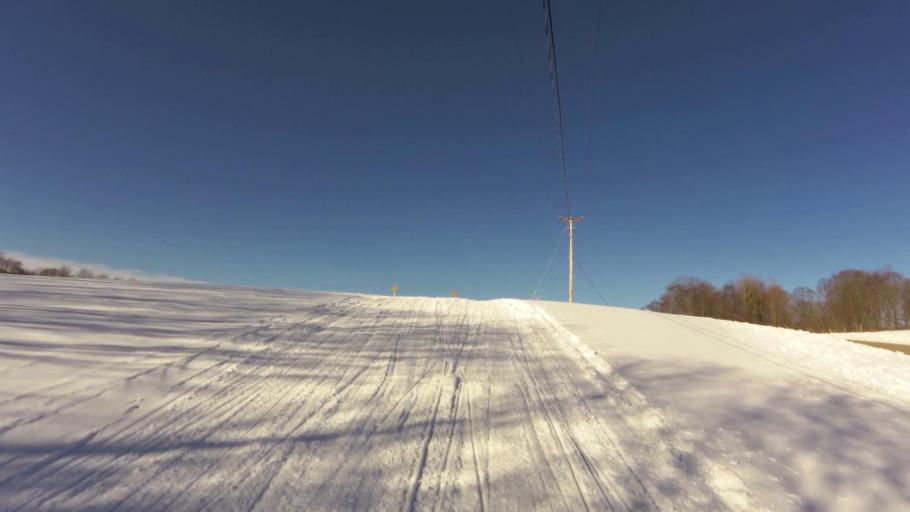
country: US
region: New York
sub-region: Cattaraugus County
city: Franklinville
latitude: 42.3918
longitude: -78.4880
